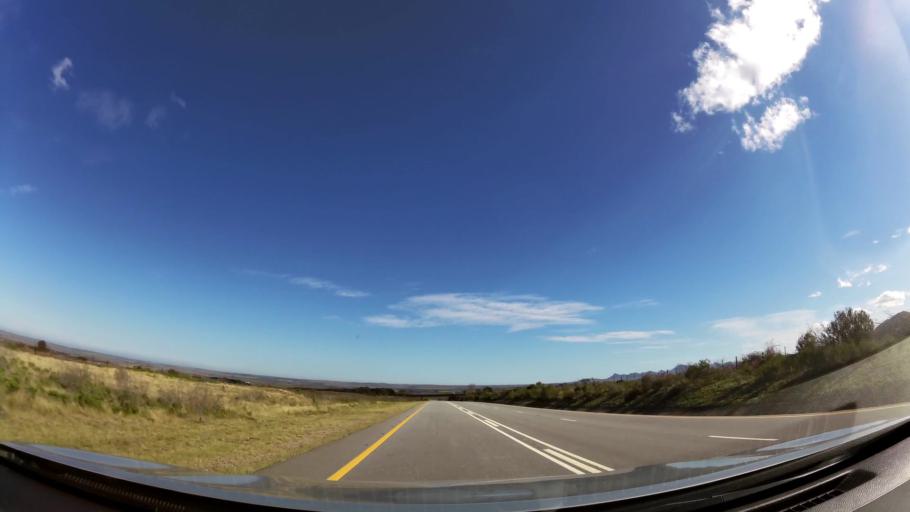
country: ZA
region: Eastern Cape
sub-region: Cacadu District Municipality
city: Kruisfontein
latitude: -33.9996
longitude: 24.6849
